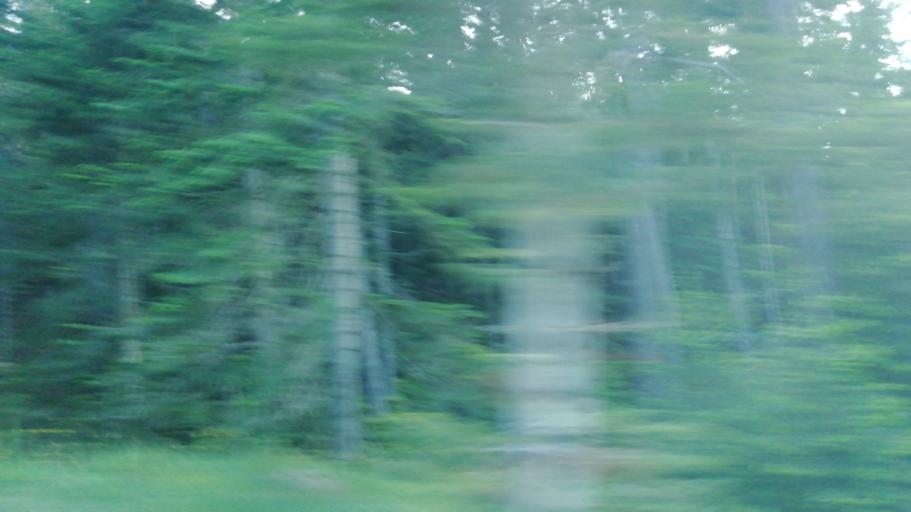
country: TR
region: Karabuk
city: Eskipazar
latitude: 41.0473
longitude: 32.5459
